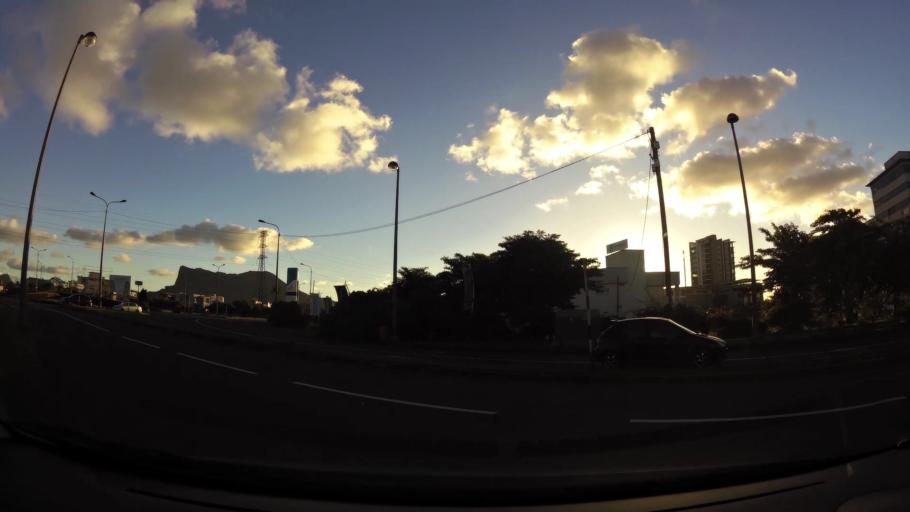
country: MU
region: Plaines Wilhems
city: Ebene
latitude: -20.2467
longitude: 57.4902
